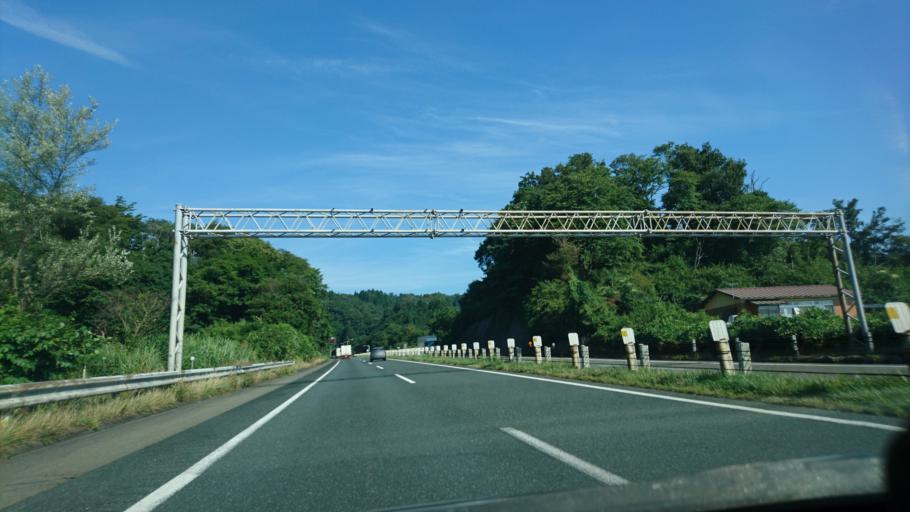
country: JP
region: Iwate
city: Ichinoseki
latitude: 38.9859
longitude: 141.1052
